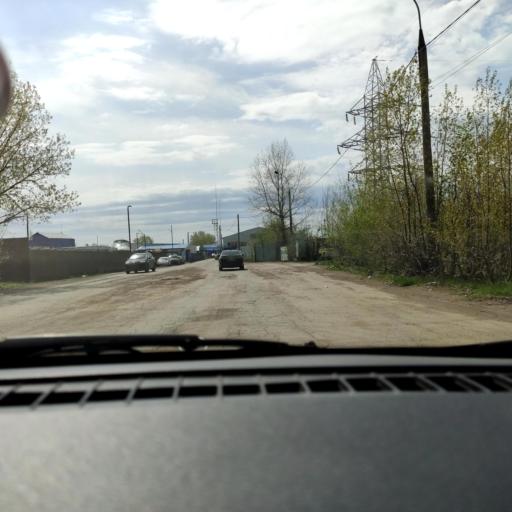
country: RU
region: Samara
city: Samara
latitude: 53.1767
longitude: 50.1237
